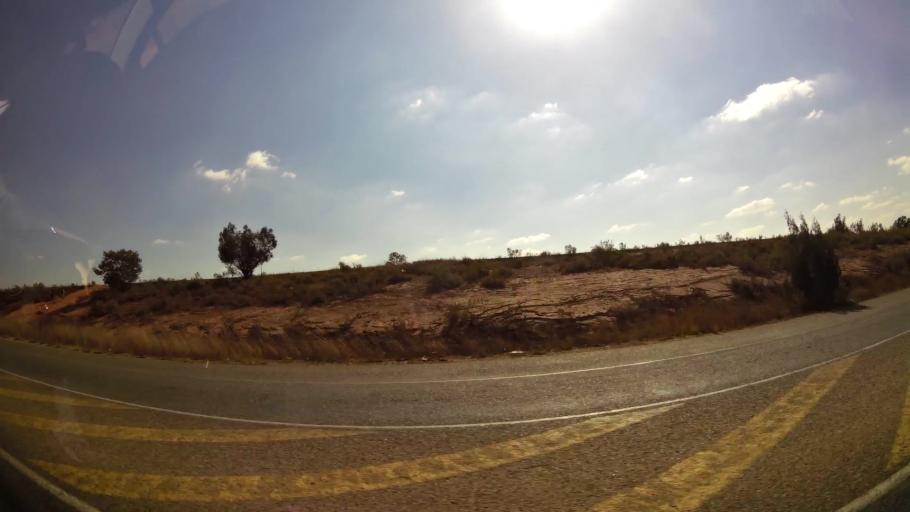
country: ZA
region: Gauteng
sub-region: West Rand District Municipality
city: Randfontein
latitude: -26.1800
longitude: 27.7583
